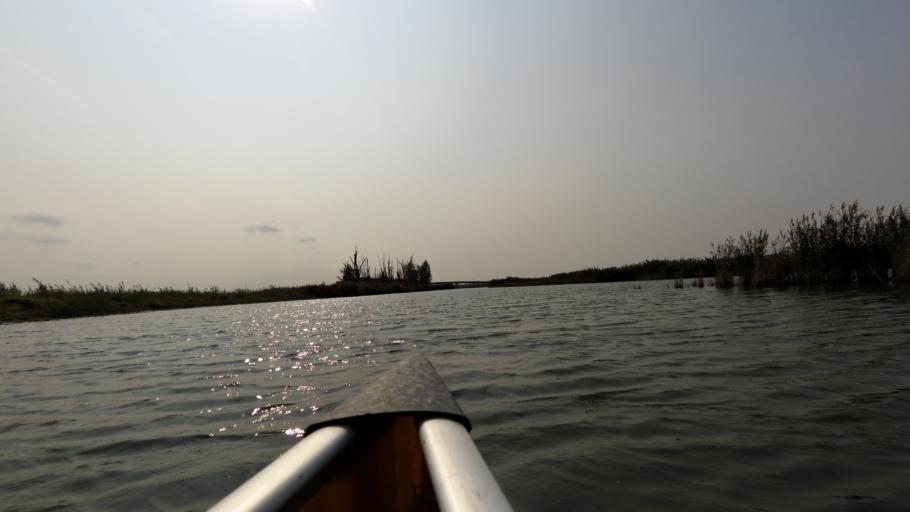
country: NL
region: South Holland
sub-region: Gemeente Sliedrecht
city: Sliedrecht
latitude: 51.7788
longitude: 4.8151
